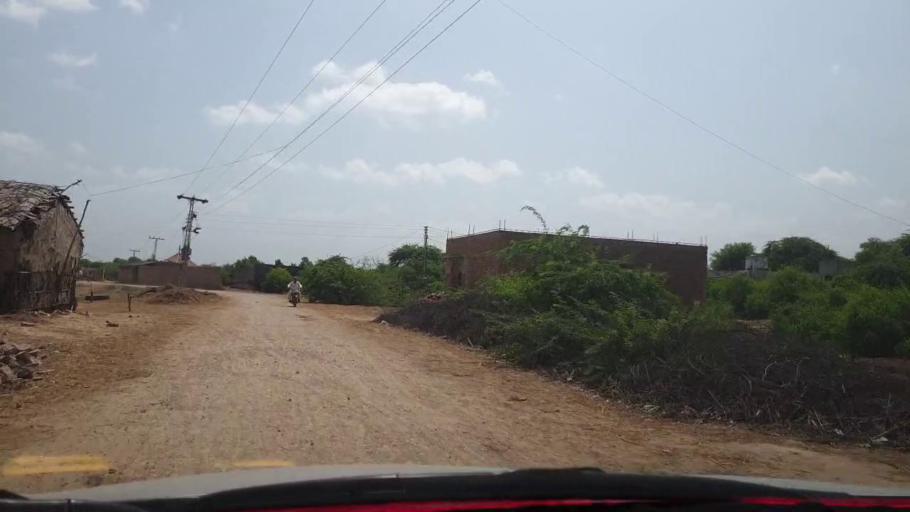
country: PK
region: Sindh
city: Talhar
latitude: 24.9042
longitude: 68.9049
